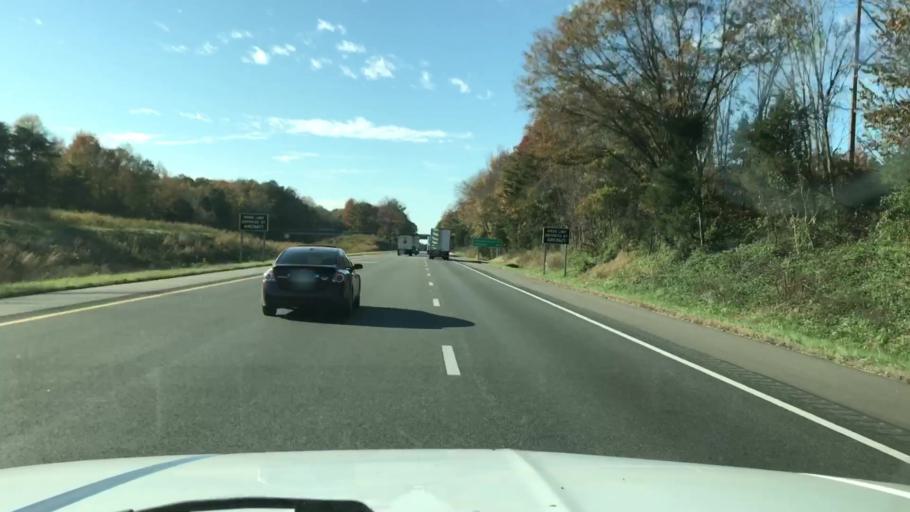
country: US
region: Virginia
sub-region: Henrico County
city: Wyndham
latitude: 37.6877
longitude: -77.6803
